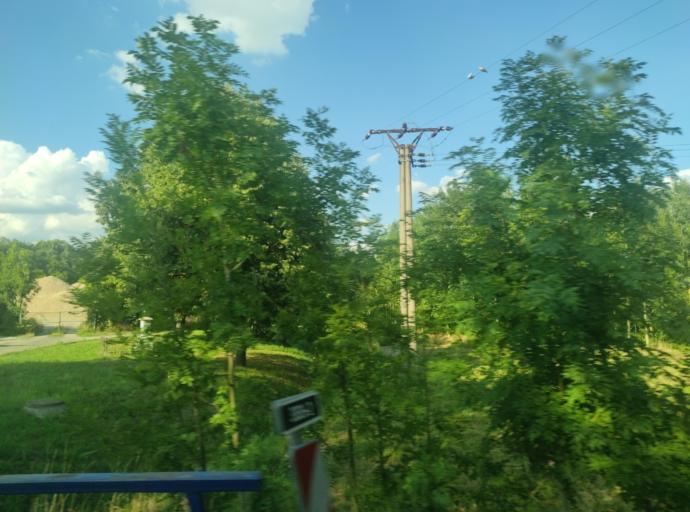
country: CZ
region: South Moravian
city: Vinicne Sumice
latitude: 49.1833
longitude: 16.8450
